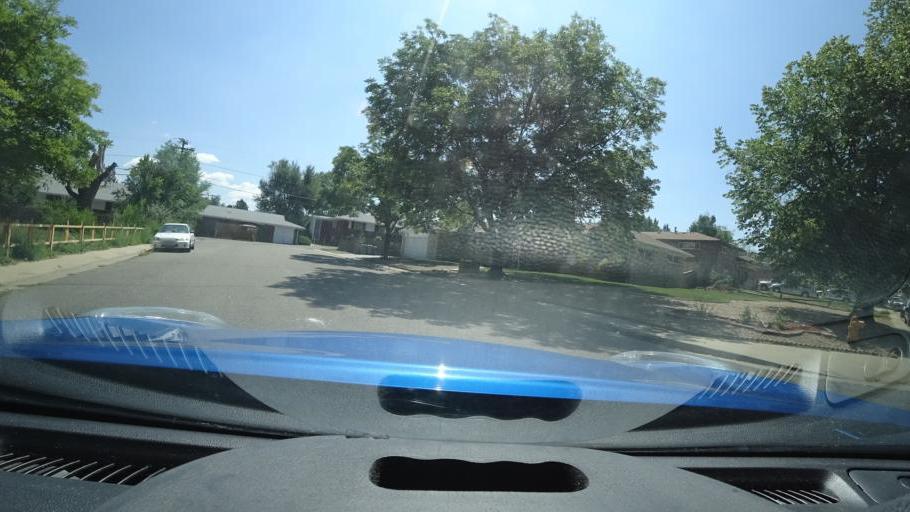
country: US
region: Colorado
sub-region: Adams County
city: Aurora
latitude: 39.7233
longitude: -104.8694
